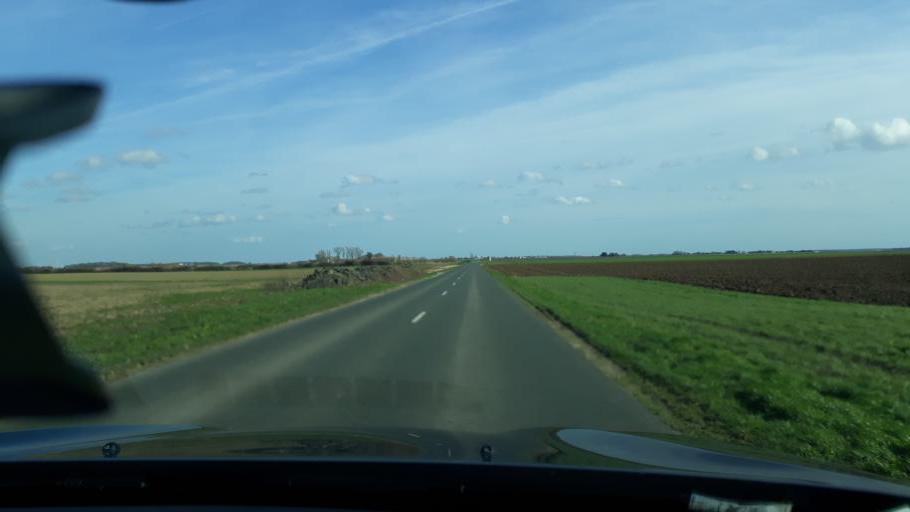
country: FR
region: Centre
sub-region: Departement du Loiret
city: Artenay
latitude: 48.0806
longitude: 1.9099
